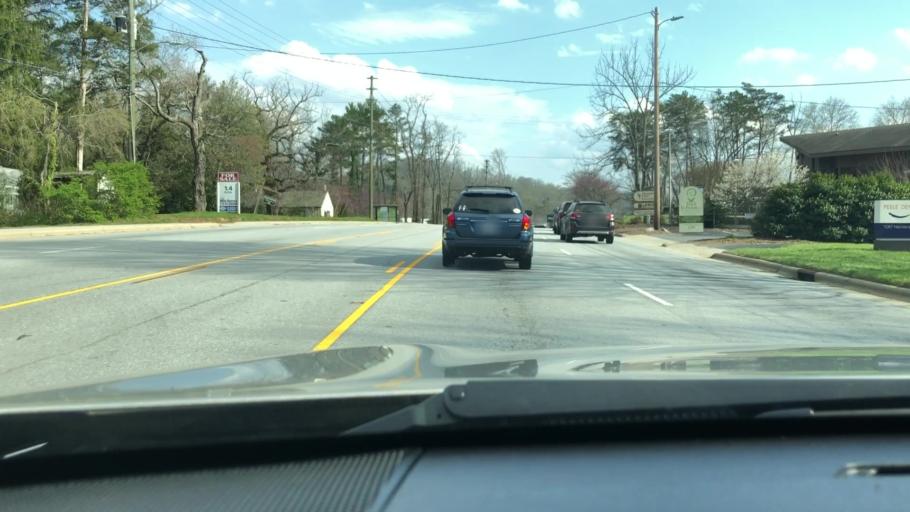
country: US
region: North Carolina
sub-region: Buncombe County
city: Biltmore Forest
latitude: 35.5358
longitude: -82.5287
